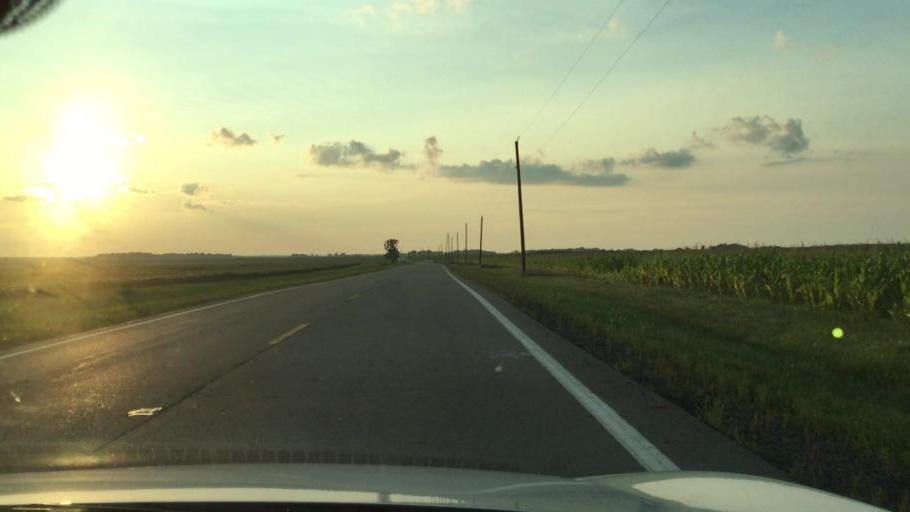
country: US
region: Ohio
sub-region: Madison County
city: Choctaw Lake
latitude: 40.0063
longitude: -83.4441
